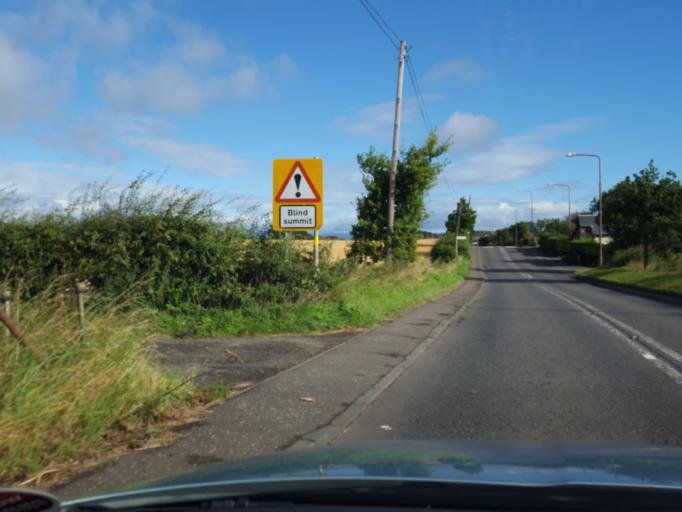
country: GB
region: Scotland
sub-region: West Lothian
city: Broxburn
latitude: 55.9615
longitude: -3.5089
